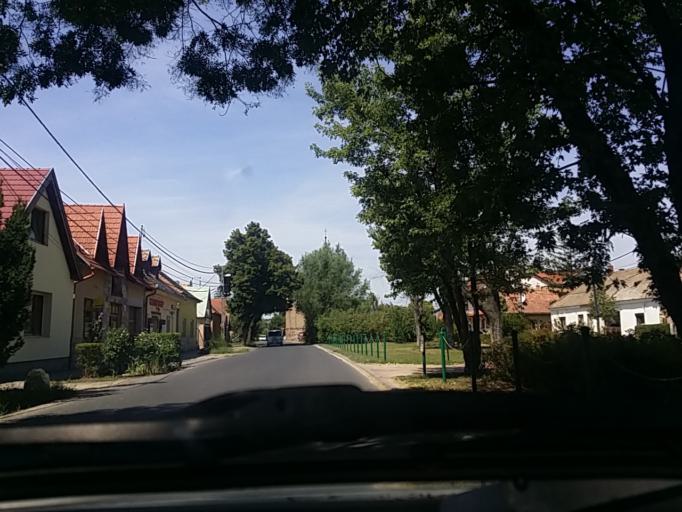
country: HU
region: Pest
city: Urom
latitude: 47.5980
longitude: 19.0161
